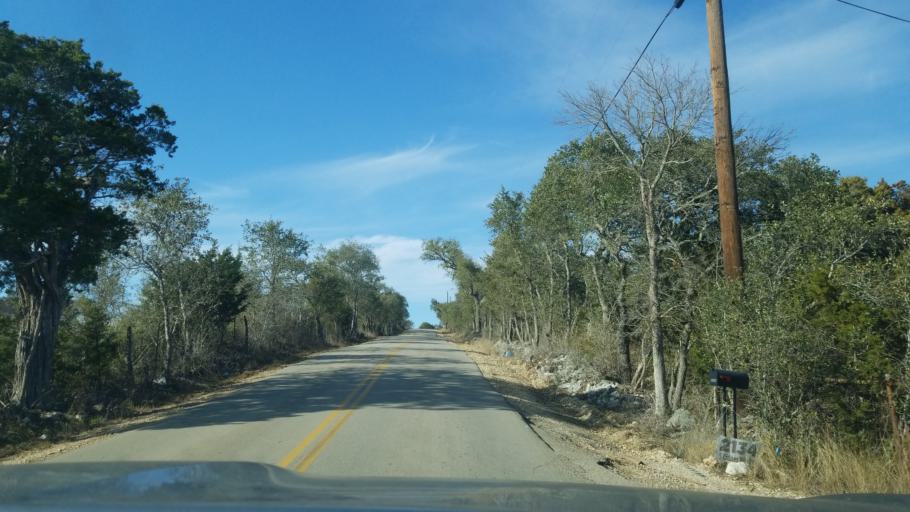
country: US
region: Texas
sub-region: Comal County
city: Canyon Lake
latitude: 29.7835
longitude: -98.2837
